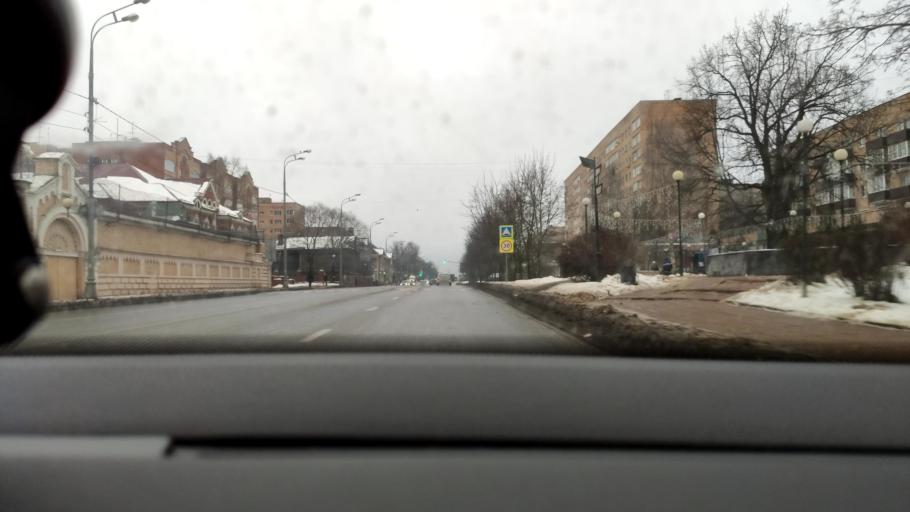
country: RU
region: Moskovskaya
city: Sergiyev Posad
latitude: 56.2995
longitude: 38.1291
